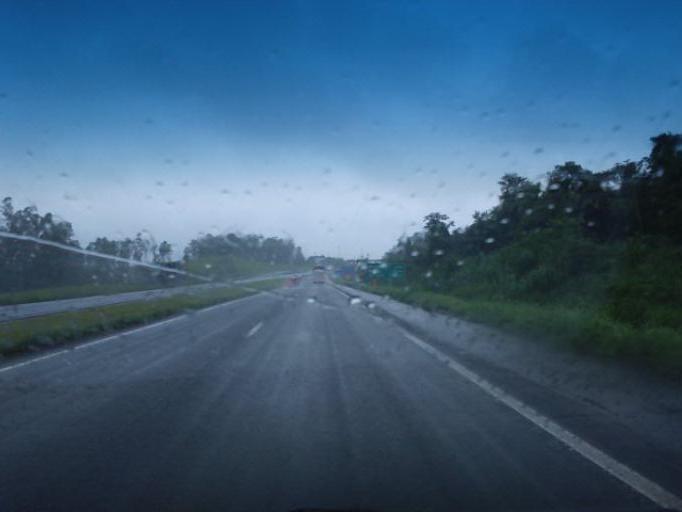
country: BR
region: Sao Paulo
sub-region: Cajati
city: Cajati
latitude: -24.7248
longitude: -48.0875
